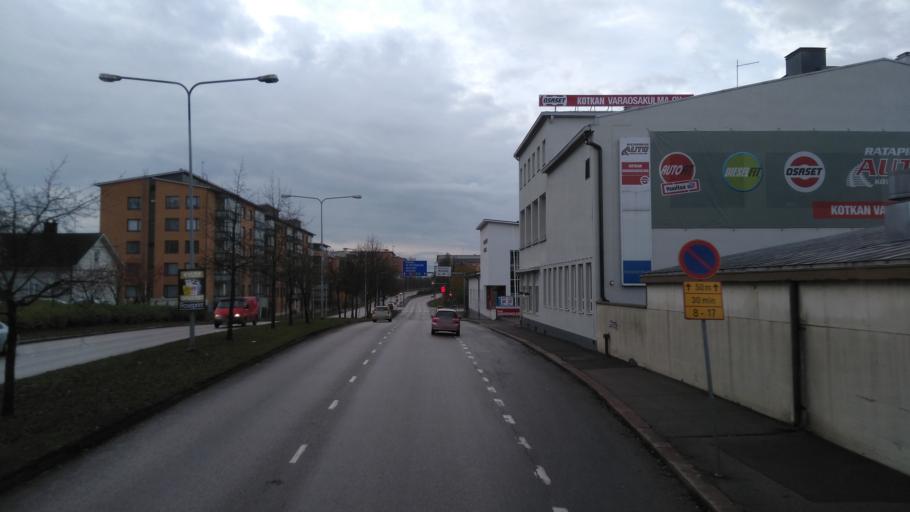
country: FI
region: Kymenlaakso
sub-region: Kotka-Hamina
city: Kotka
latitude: 60.4641
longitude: 26.9308
